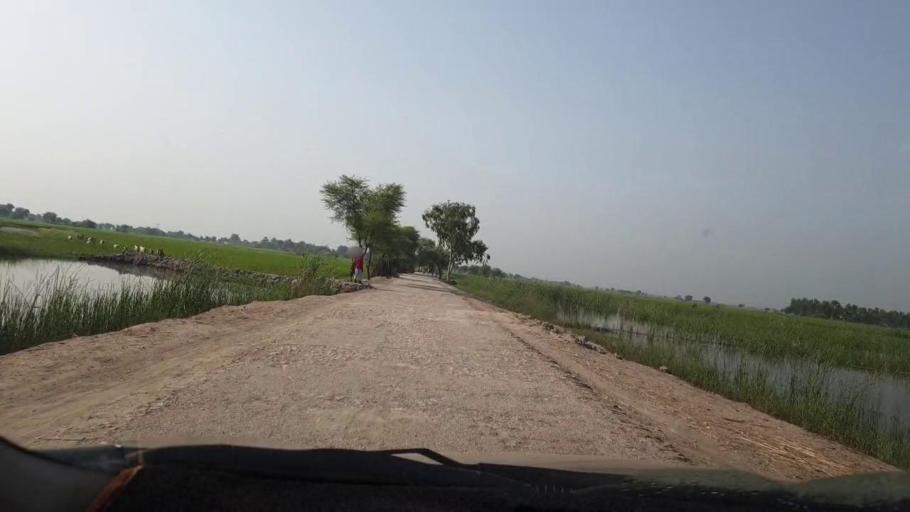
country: PK
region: Sindh
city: Goth Garelo
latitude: 27.4699
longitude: 68.0887
